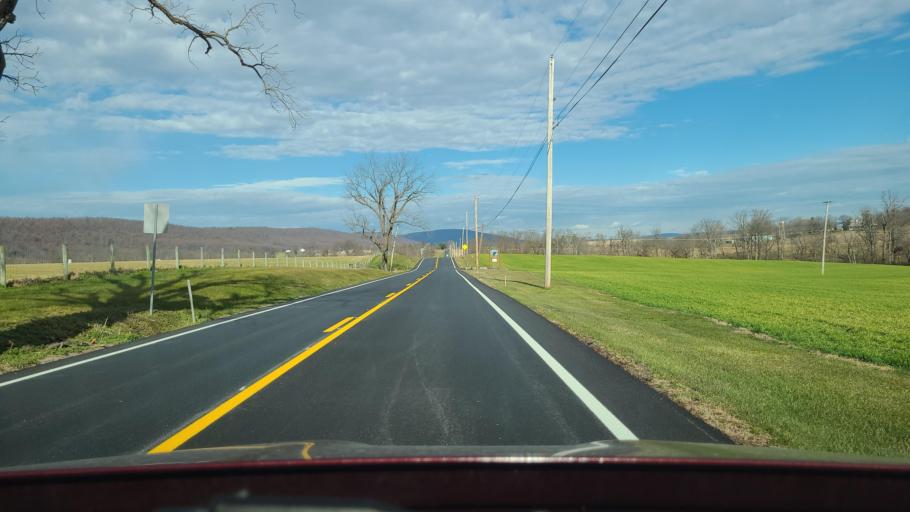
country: US
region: Maryland
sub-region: Frederick County
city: Brunswick
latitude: 39.3534
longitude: -77.6384
